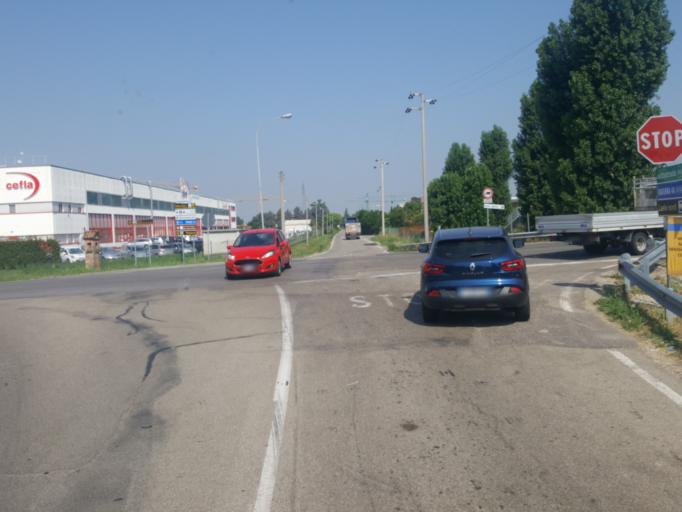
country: IT
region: Emilia-Romagna
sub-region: Provincia di Bologna
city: Imola
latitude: 44.3831
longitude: 11.7309
